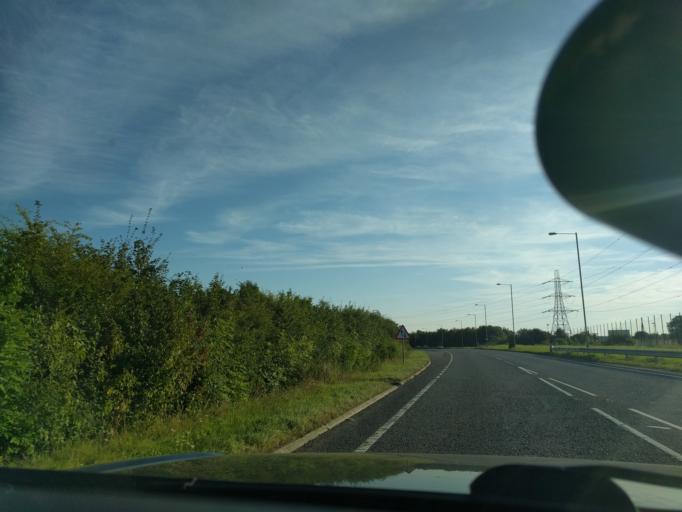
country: GB
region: England
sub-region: Wiltshire
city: Chippenham
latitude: 51.4664
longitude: -2.1468
